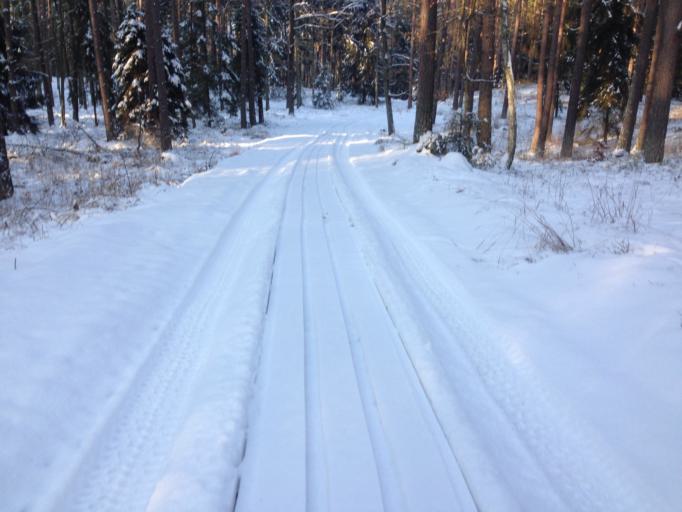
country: PL
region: Kujawsko-Pomorskie
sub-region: Powiat brodnicki
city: Gorzno
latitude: 53.1902
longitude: 19.6919
